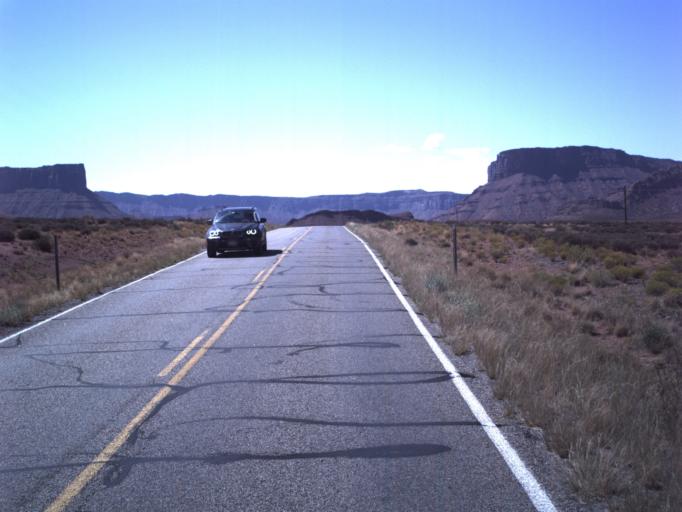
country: US
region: Utah
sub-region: Grand County
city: Moab
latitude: 38.7192
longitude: -109.3642
